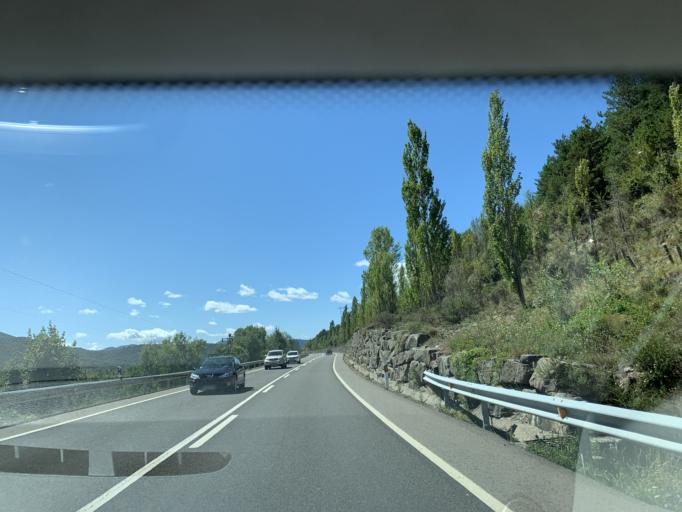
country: ES
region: Aragon
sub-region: Provincia de Huesca
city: Biescas
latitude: 42.5749
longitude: -0.3243
